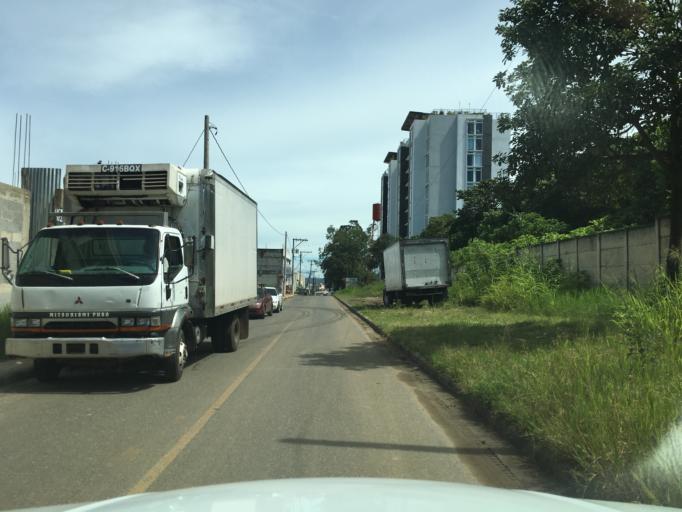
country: GT
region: Guatemala
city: Mixco
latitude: 14.6563
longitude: -90.5634
